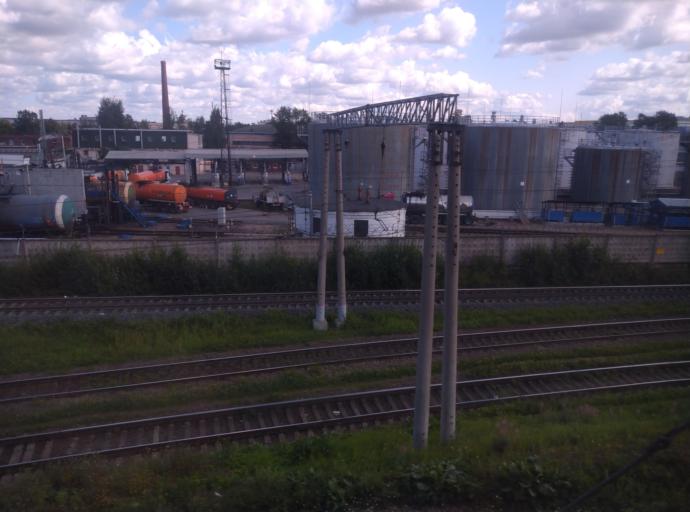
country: RU
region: St.-Petersburg
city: Centralniy
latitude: 59.9008
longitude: 30.3828
